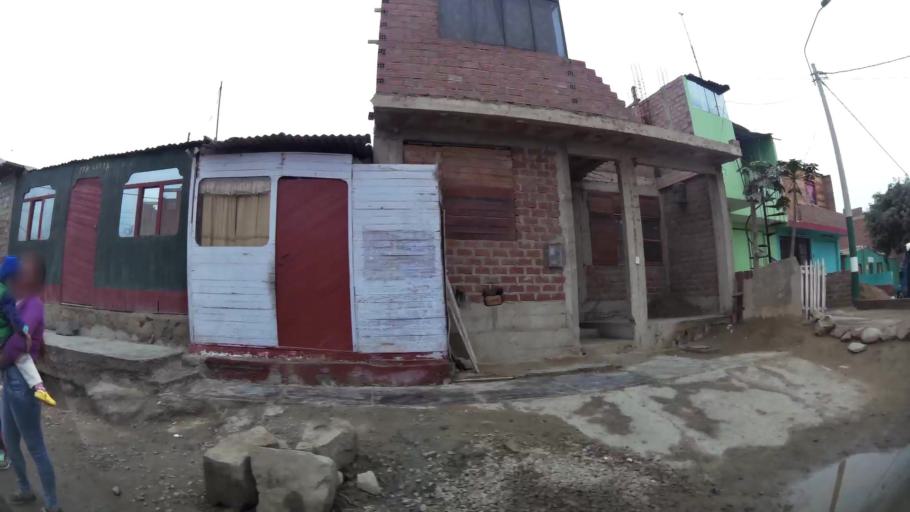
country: PE
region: Lima
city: Ventanilla
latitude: -11.8796
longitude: -77.1337
